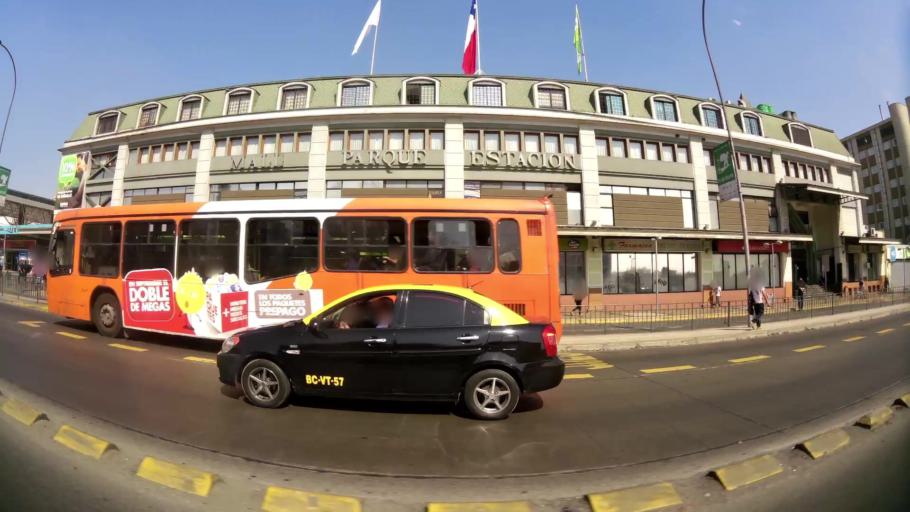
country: CL
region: Santiago Metropolitan
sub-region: Provincia de Santiago
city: Santiago
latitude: -33.4530
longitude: -70.6868
